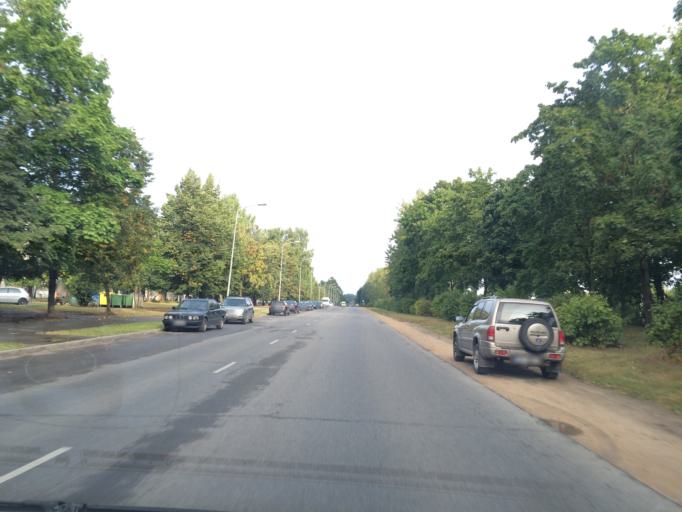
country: LV
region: Kekava
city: Kekava
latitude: 56.9063
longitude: 24.2069
